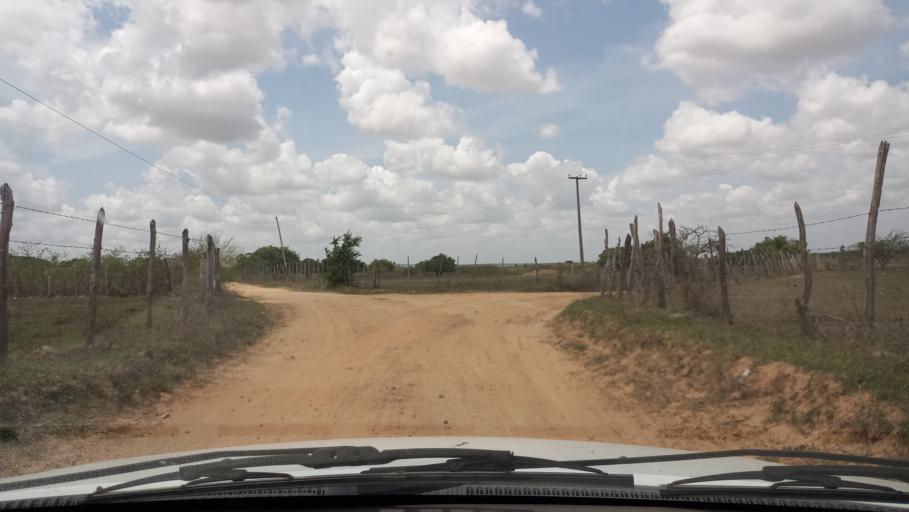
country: BR
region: Rio Grande do Norte
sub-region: Brejinho
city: Brejinho
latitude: -6.2766
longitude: -35.3474
